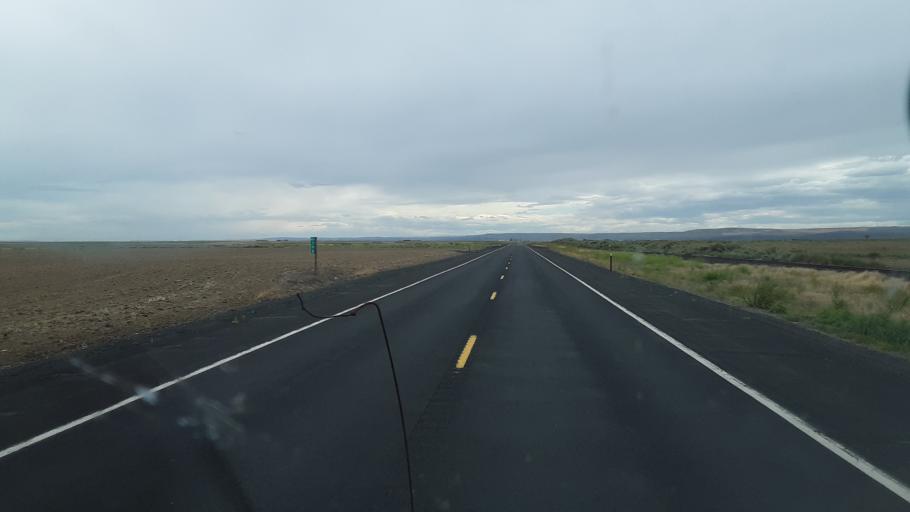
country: US
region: Washington
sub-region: Okanogan County
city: Coulee Dam
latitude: 47.6693
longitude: -119.1787
